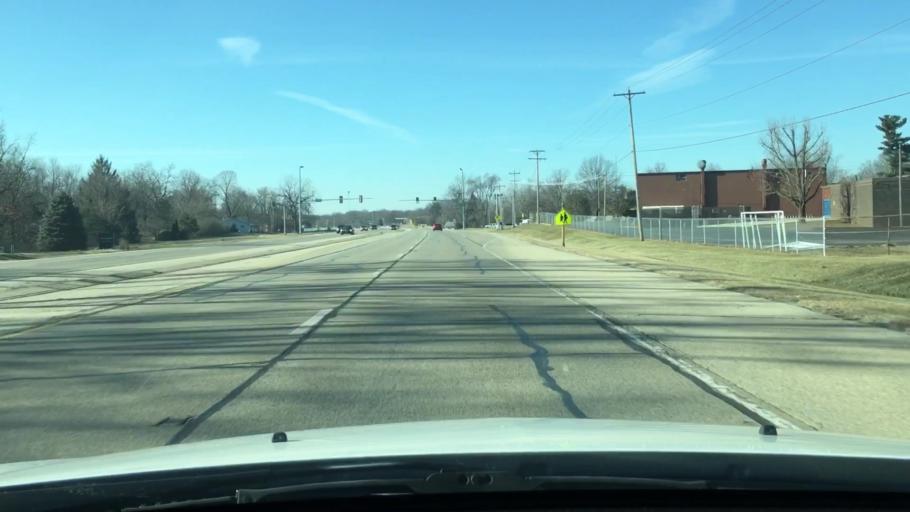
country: US
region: Illinois
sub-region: Woodford County
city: Germantown Hills
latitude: 40.7671
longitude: -89.4649
